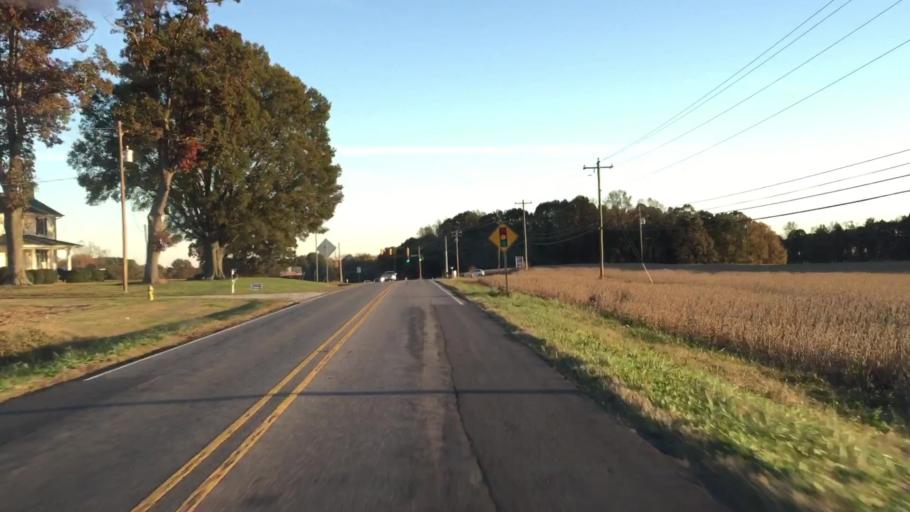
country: US
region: North Carolina
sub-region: Iredell County
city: Mooresville
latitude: 35.5626
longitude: -80.7893
